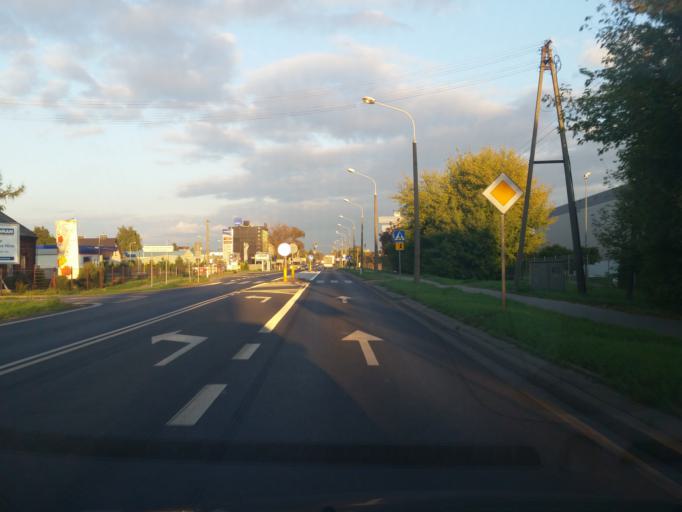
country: PL
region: Masovian Voivodeship
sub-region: Powiat warszawski zachodni
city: Ozarow Mazowiecki
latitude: 52.2110
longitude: 20.7739
